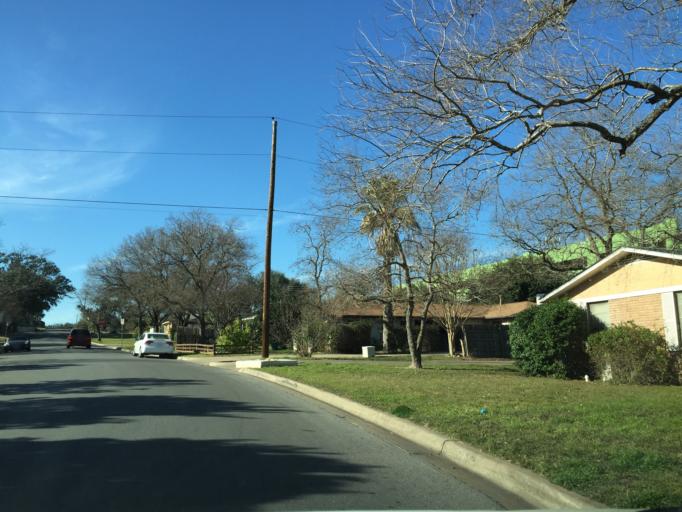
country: US
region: Texas
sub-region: Travis County
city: Austin
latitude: 30.2354
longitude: -97.7516
